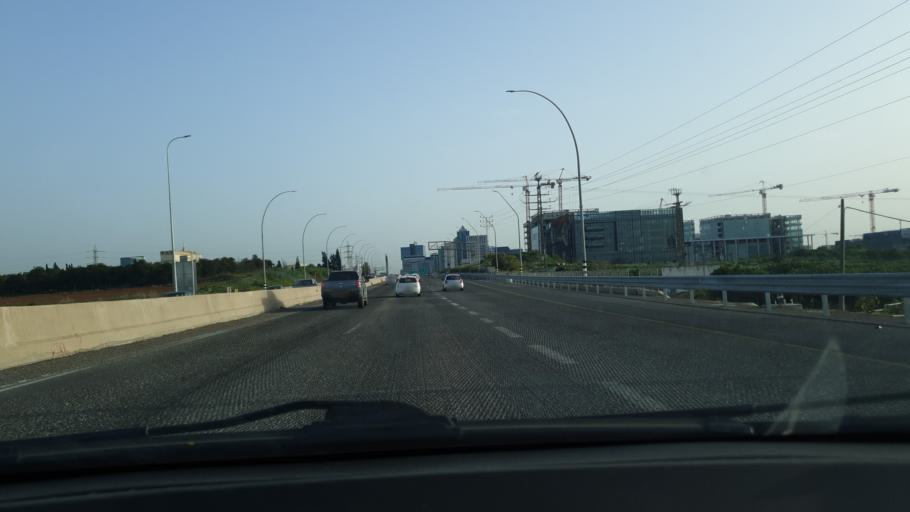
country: IL
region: Central District
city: Ra'anana
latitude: 32.2051
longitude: 34.8841
